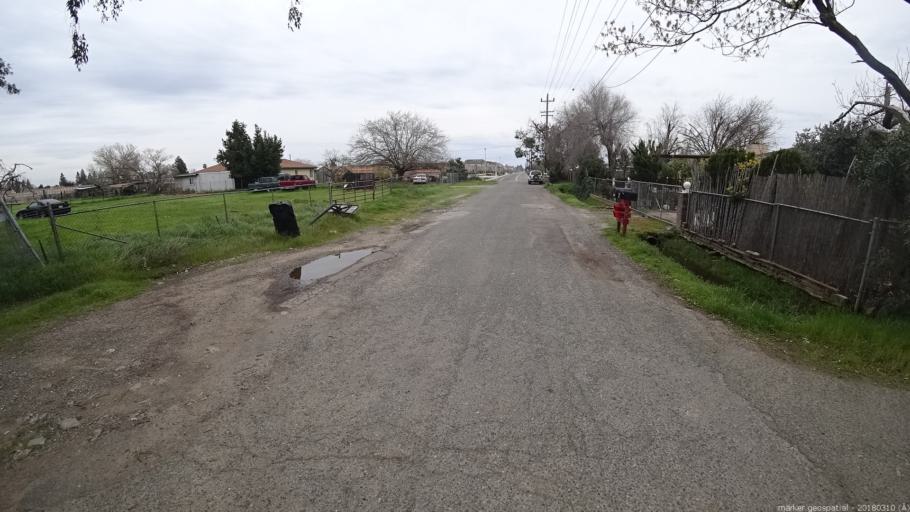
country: US
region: California
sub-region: Sacramento County
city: Florin
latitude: 38.4726
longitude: -121.3843
